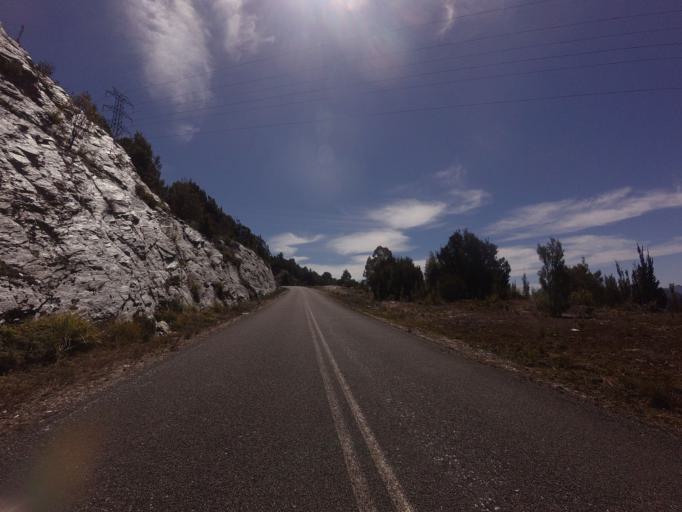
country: AU
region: Tasmania
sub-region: West Coast
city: Queenstown
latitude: -42.7562
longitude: 146.0021
